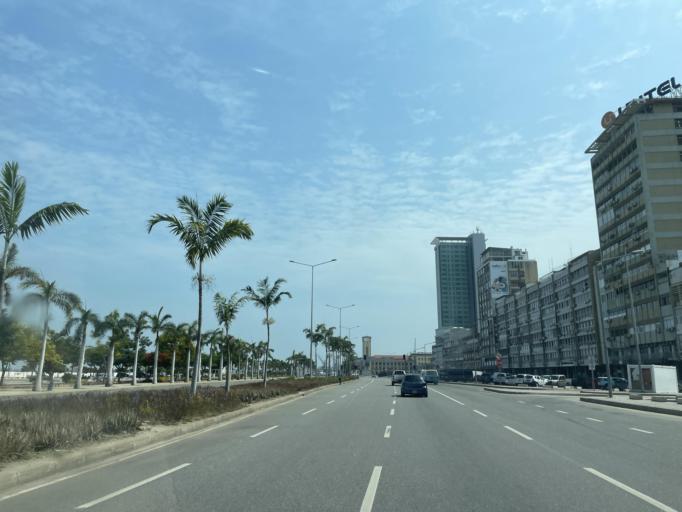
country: AO
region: Luanda
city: Luanda
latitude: -8.8058
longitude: 13.2399
